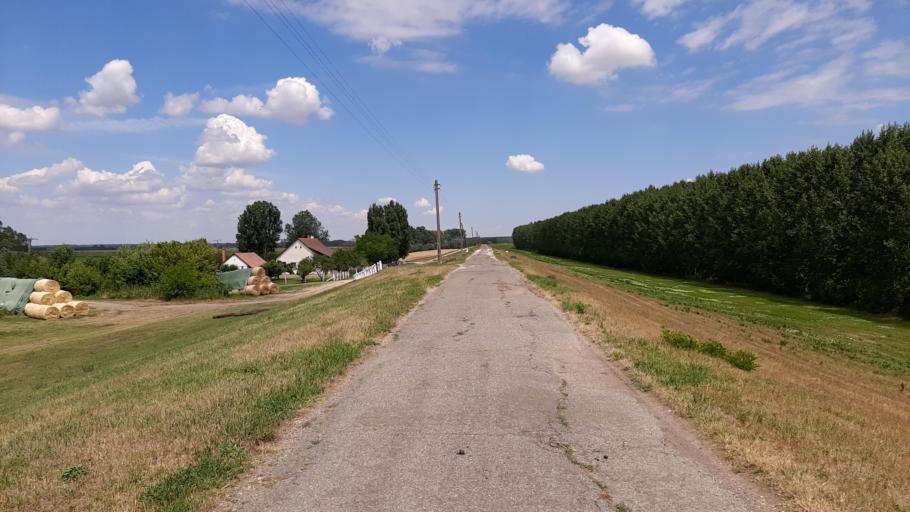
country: HU
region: Csongrad
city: Csongrad
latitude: 46.6507
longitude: 20.1836
